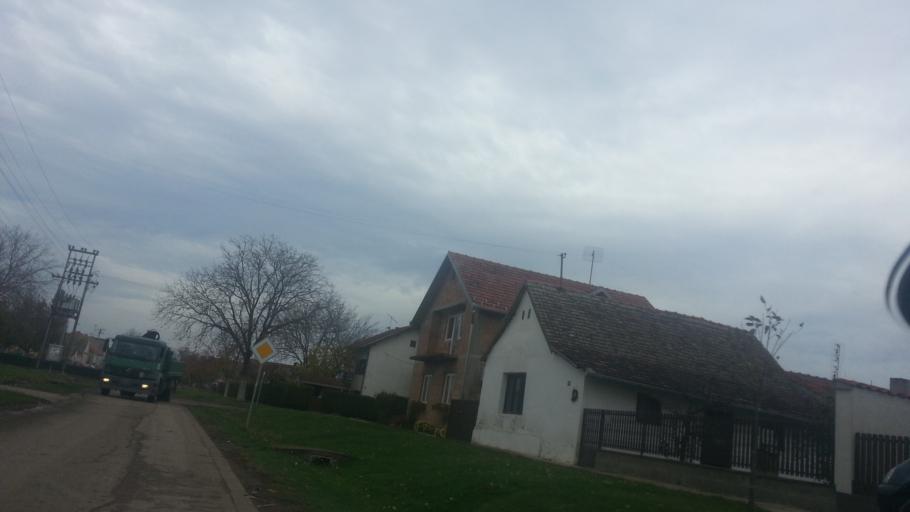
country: RS
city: Golubinci
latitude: 44.9937
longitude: 20.0663
